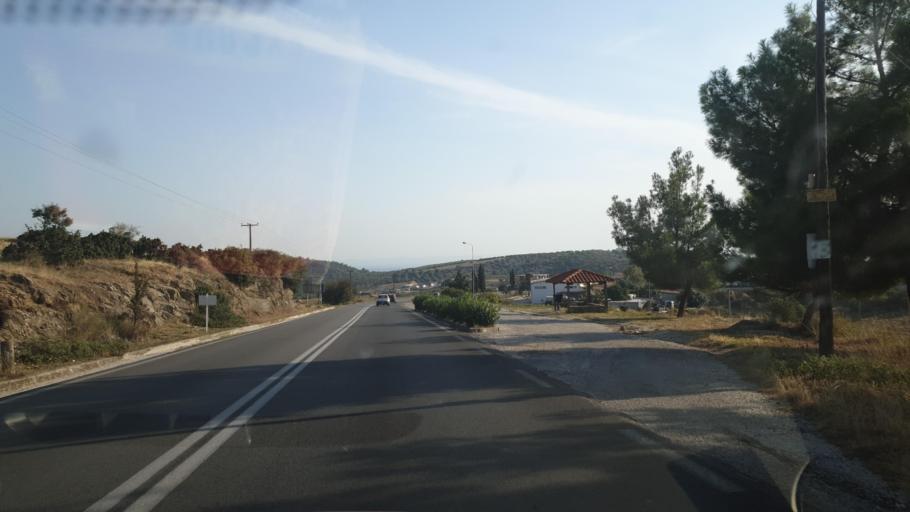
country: GR
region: Central Macedonia
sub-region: Nomos Chalkidikis
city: Nikiti
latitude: 40.2174
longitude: 23.6971
